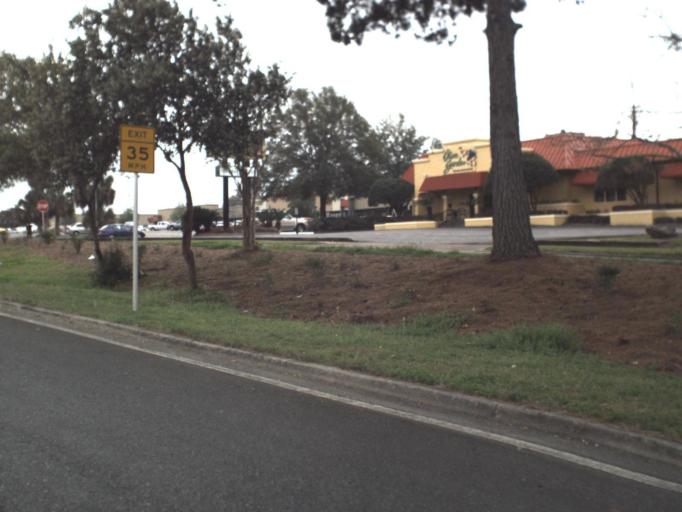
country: US
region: Florida
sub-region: Leon County
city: Tallahassee
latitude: 30.4379
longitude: -84.2665
